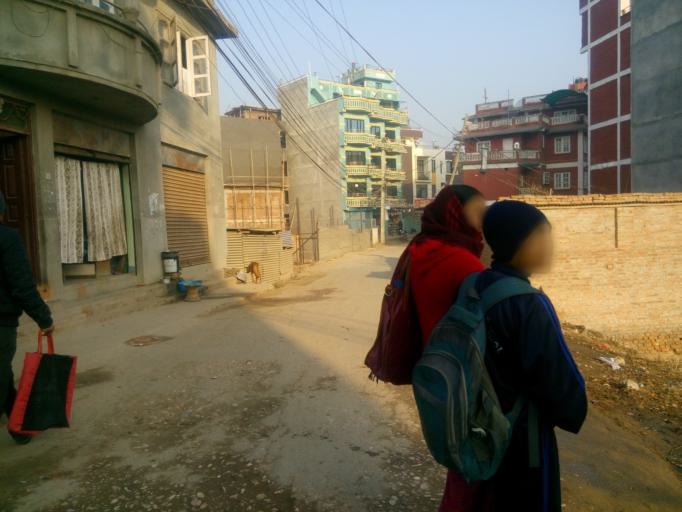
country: NP
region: Central Region
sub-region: Bagmati Zone
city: Patan
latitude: 27.6610
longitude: 85.3367
